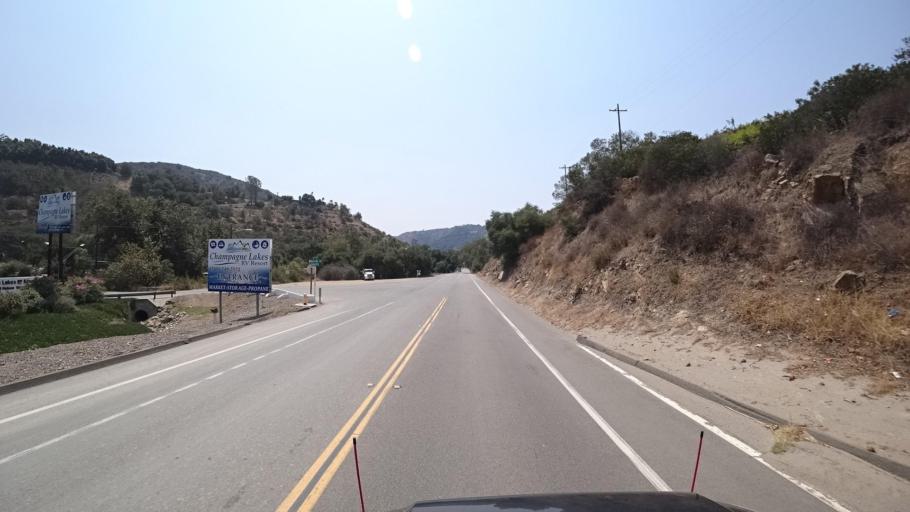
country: US
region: California
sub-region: San Diego County
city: Hidden Meadows
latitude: 33.2757
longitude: -117.1517
